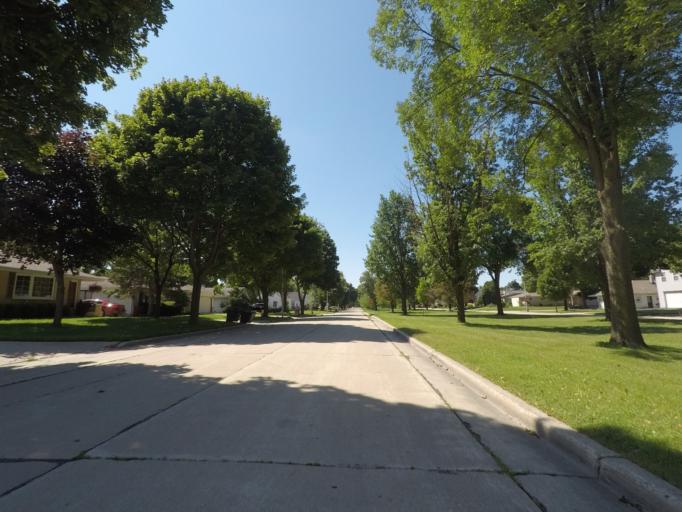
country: US
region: Wisconsin
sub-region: Waukesha County
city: Elm Grove
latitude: 43.0208
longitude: -88.0620
